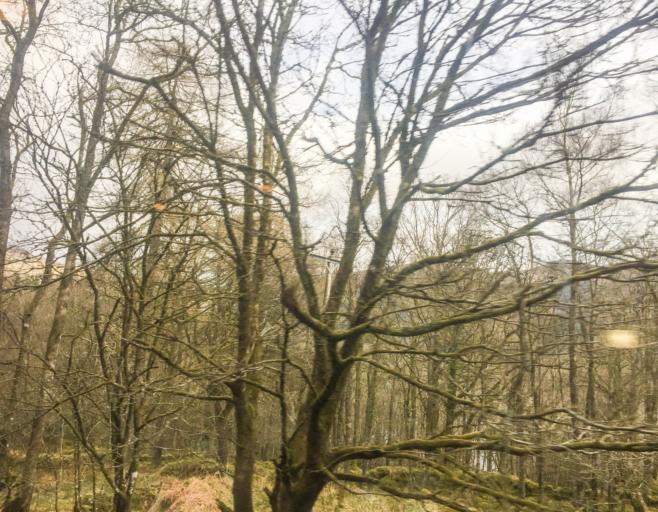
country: GB
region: Scotland
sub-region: Argyll and Bute
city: Garelochhead
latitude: 56.2102
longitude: -4.7040
